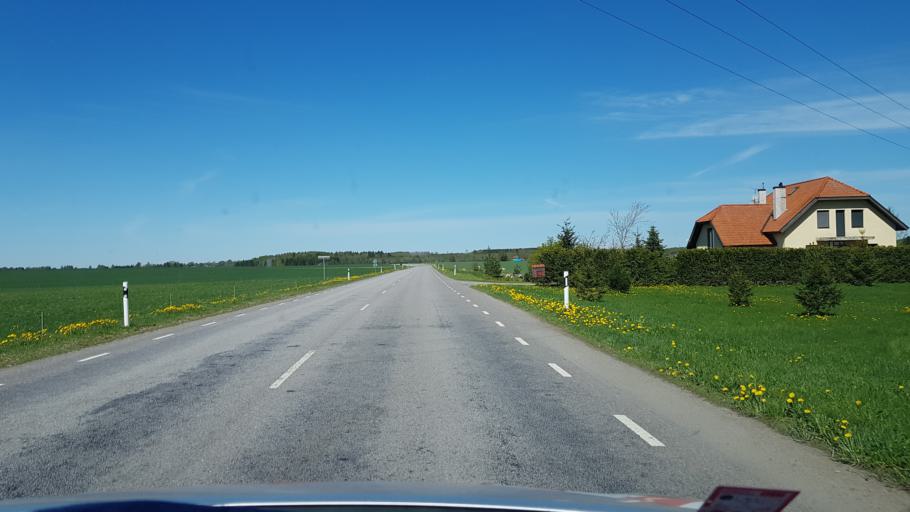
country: EE
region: Tartu
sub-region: Tartu linn
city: Tartu
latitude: 58.3828
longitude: 26.6152
